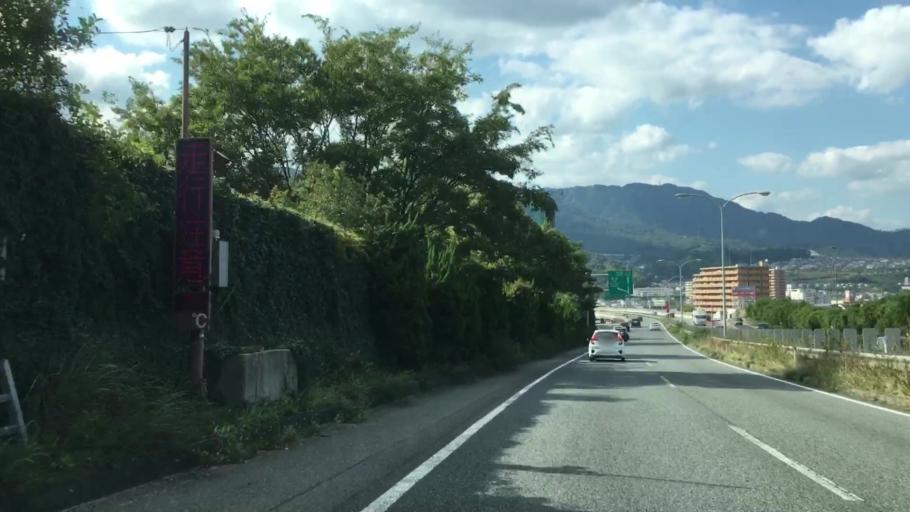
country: JP
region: Hiroshima
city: Hatsukaichi
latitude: 34.3772
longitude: 132.3669
